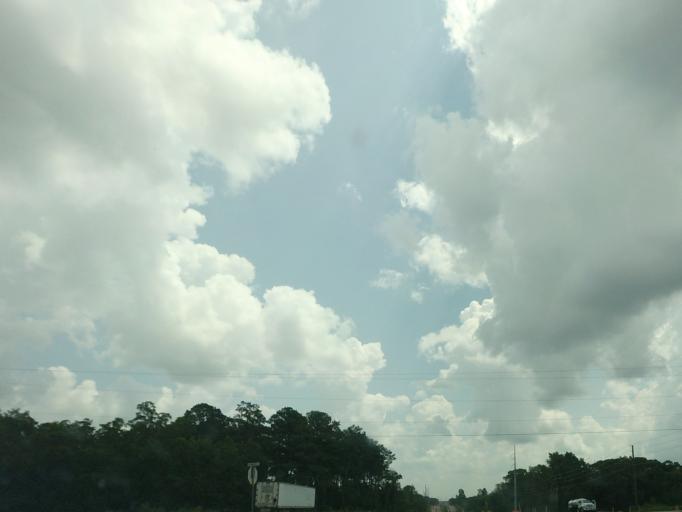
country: US
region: Georgia
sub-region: Houston County
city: Perry
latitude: 32.5464
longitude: -83.7297
